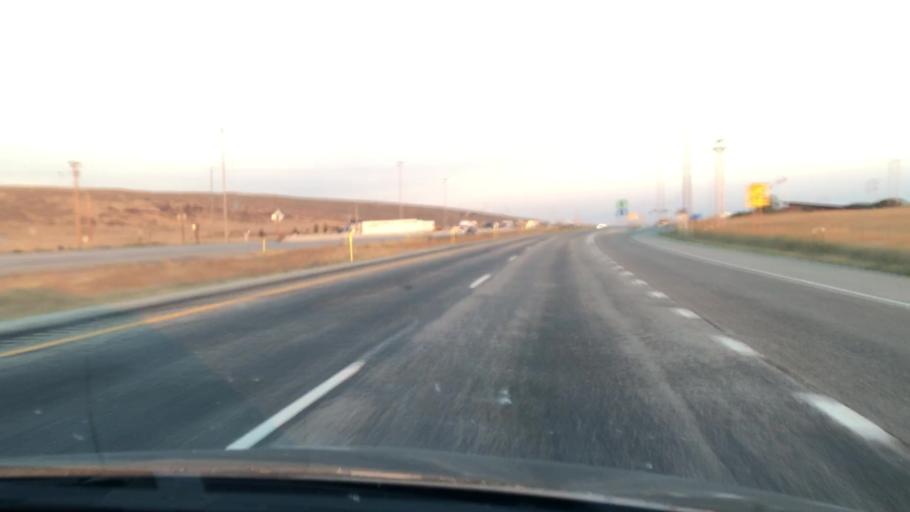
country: US
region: Idaho
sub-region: Minidoka County
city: Rupert
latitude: 42.5068
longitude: -113.4105
